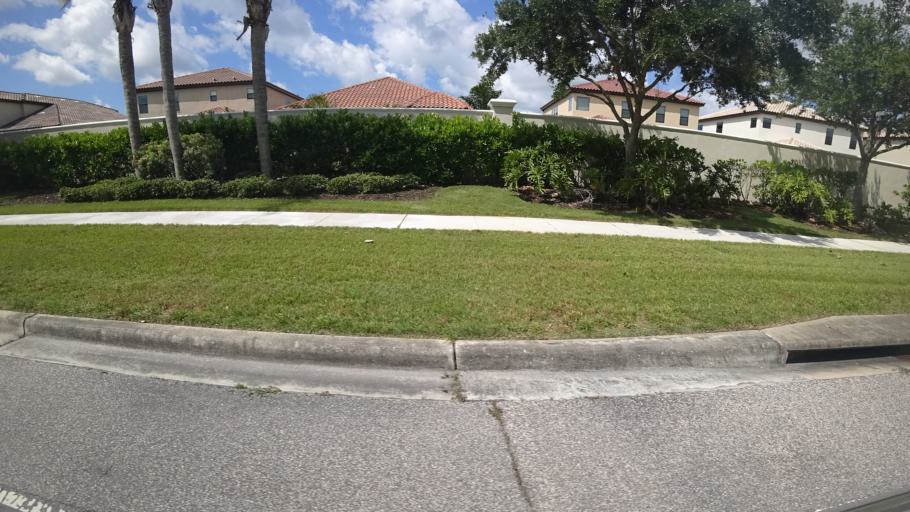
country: US
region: Florida
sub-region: Manatee County
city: Bayshore Gardens
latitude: 27.4331
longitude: -82.6197
